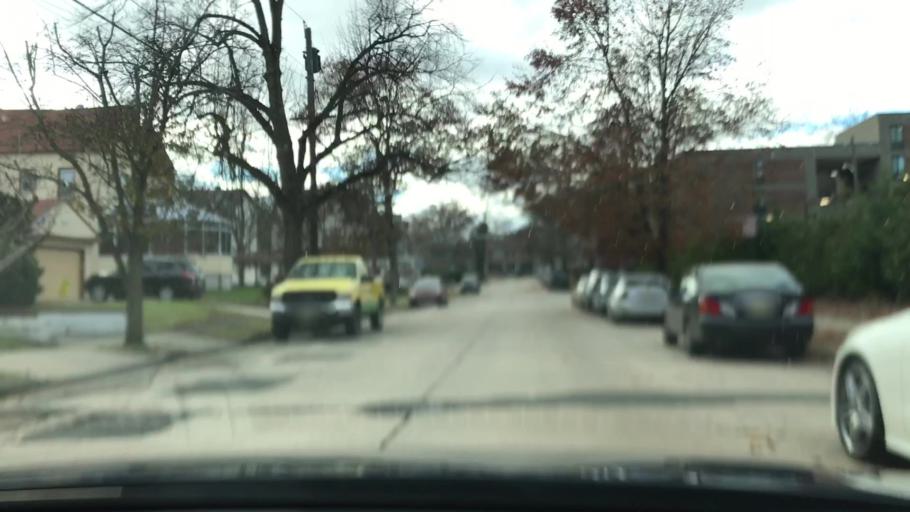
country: US
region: New Jersey
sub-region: Bergen County
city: Rutherford
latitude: 40.8302
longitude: -74.1103
